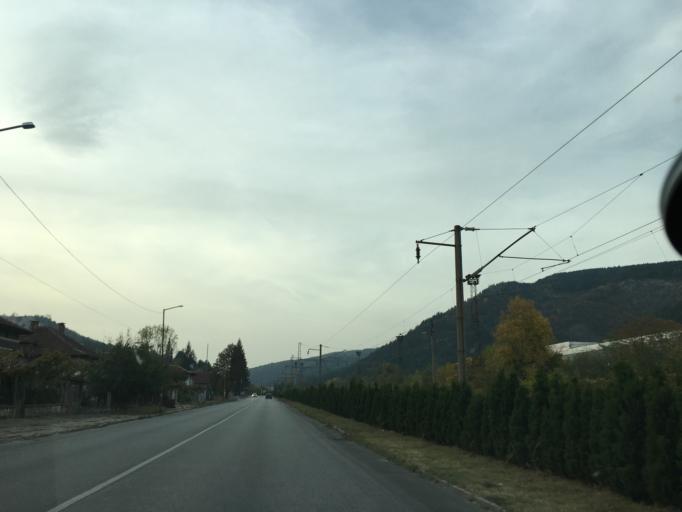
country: BG
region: Pazardzhik
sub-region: Obshtina Belovo
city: Belovo
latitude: 42.2189
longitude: 24.0051
